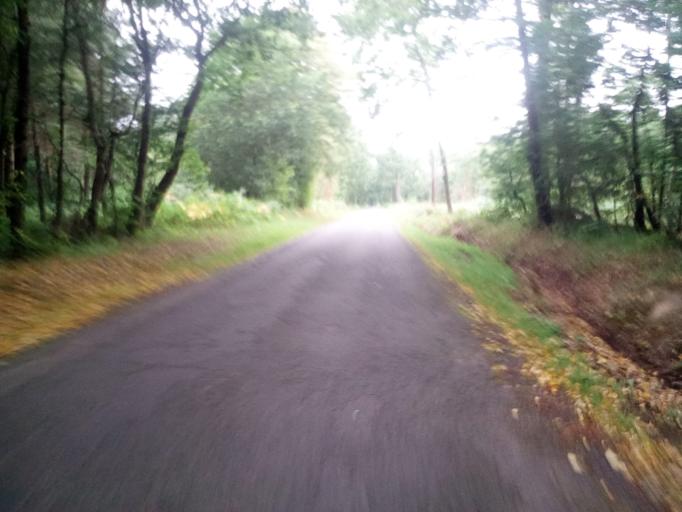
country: FR
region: Lower Normandy
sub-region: Departement du Calvados
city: Clinchamps-sur-Orne
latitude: 49.0259
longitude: -0.3962
